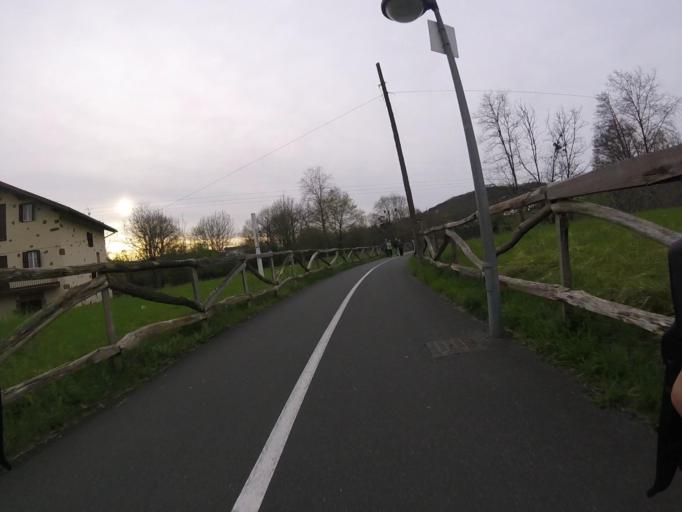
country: ES
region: Basque Country
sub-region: Provincia de Guipuzcoa
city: Lezo
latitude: 43.2924
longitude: -1.8485
